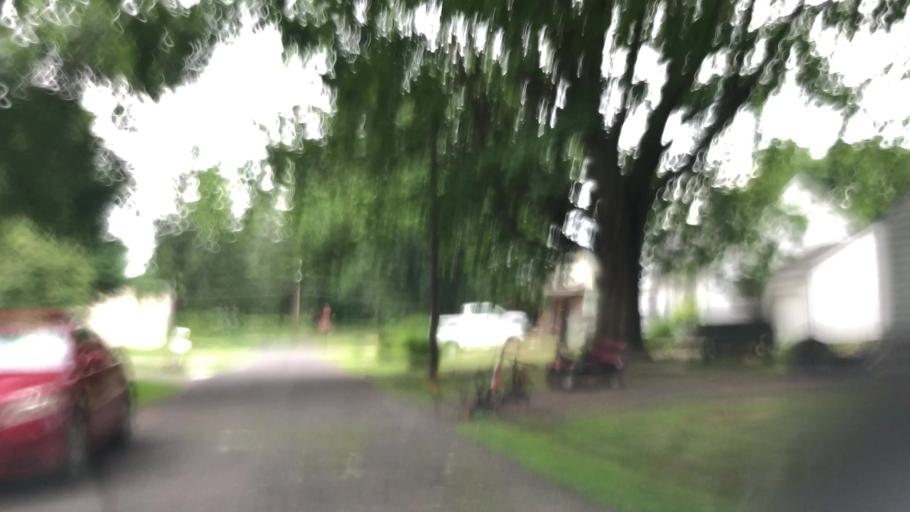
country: US
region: Ohio
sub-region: Stark County
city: North Canton
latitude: 40.8507
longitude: -81.3877
